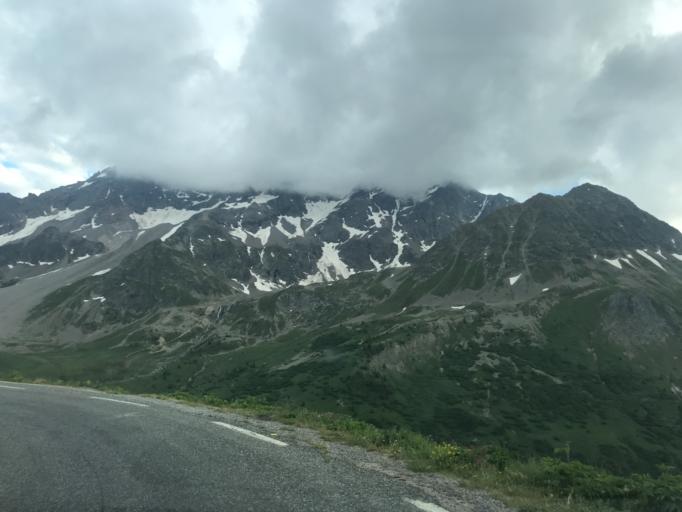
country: FR
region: Provence-Alpes-Cote d'Azur
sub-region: Departement des Hautes-Alpes
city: Le Monetier-les-Bains
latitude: 45.0383
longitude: 6.3923
